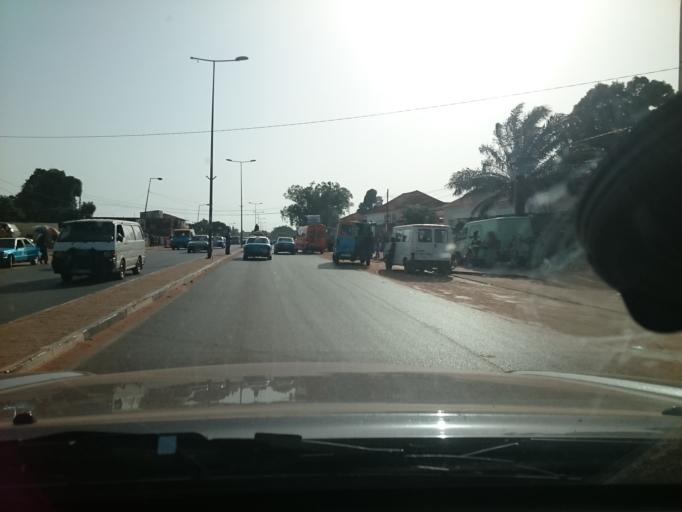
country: GW
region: Bissau
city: Bissau
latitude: 11.8584
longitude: -15.6024
